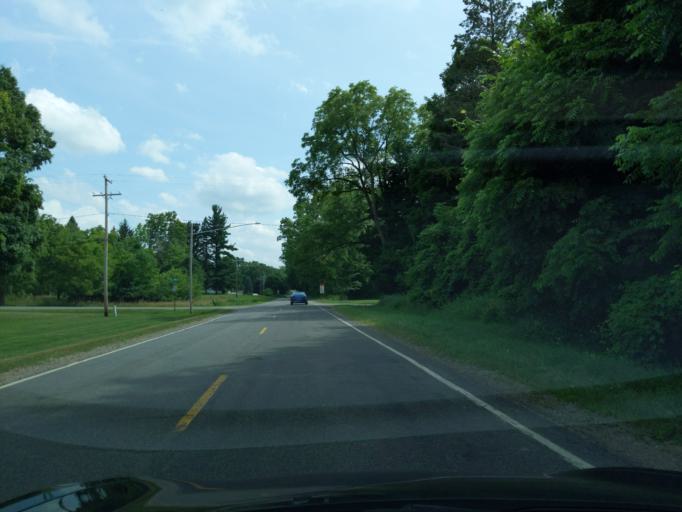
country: US
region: Michigan
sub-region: Eaton County
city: Dimondale
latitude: 42.6263
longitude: -84.6029
